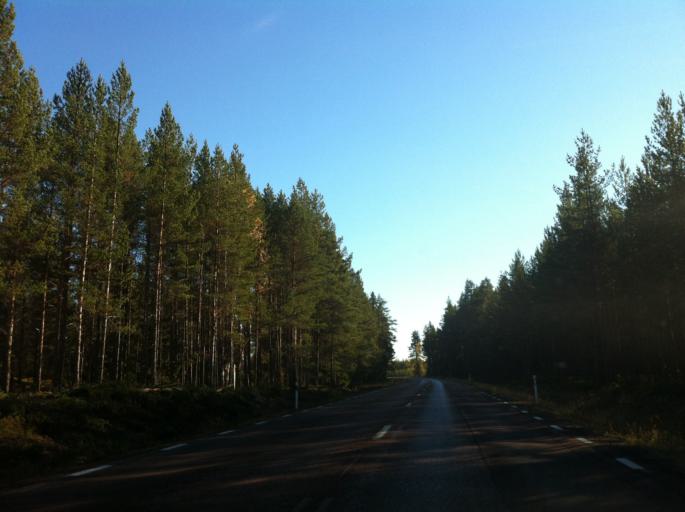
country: SE
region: Dalarna
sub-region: Alvdalens Kommun
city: AElvdalen
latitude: 61.1677
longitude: 14.1087
